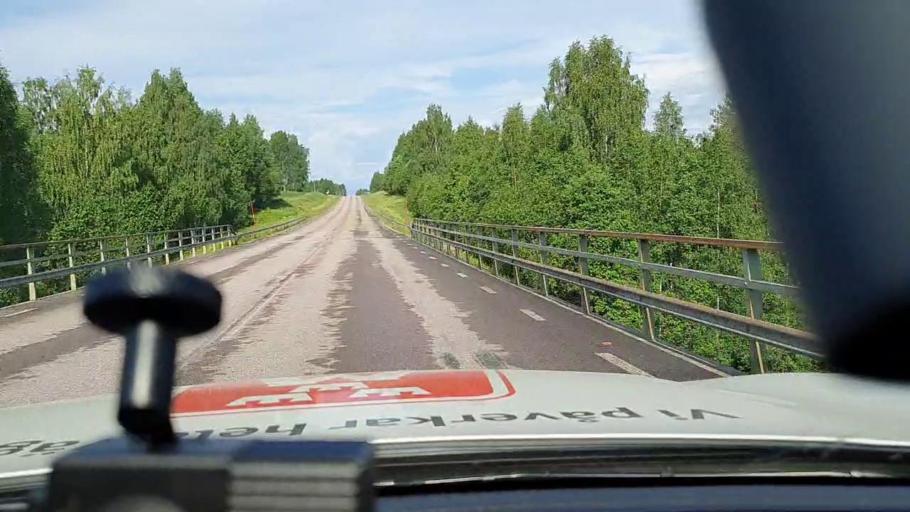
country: SE
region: Norrbotten
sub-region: Alvsbyns Kommun
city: AElvsbyn
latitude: 66.0136
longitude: 21.1681
